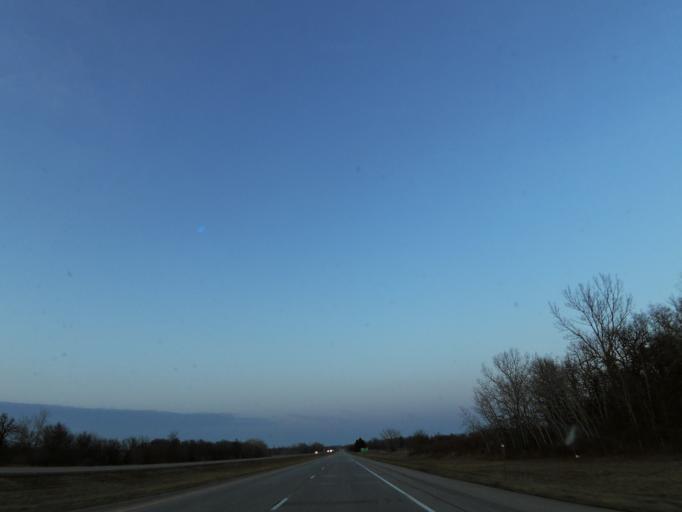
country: US
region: Minnesota
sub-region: Mower County
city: Grand Meadow
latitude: 43.6811
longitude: -92.7406
